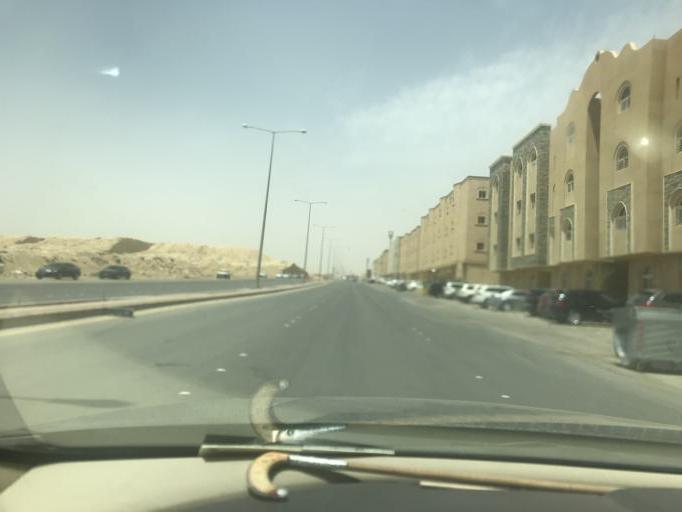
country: SA
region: Ar Riyad
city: Riyadh
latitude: 24.7918
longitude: 46.6696
